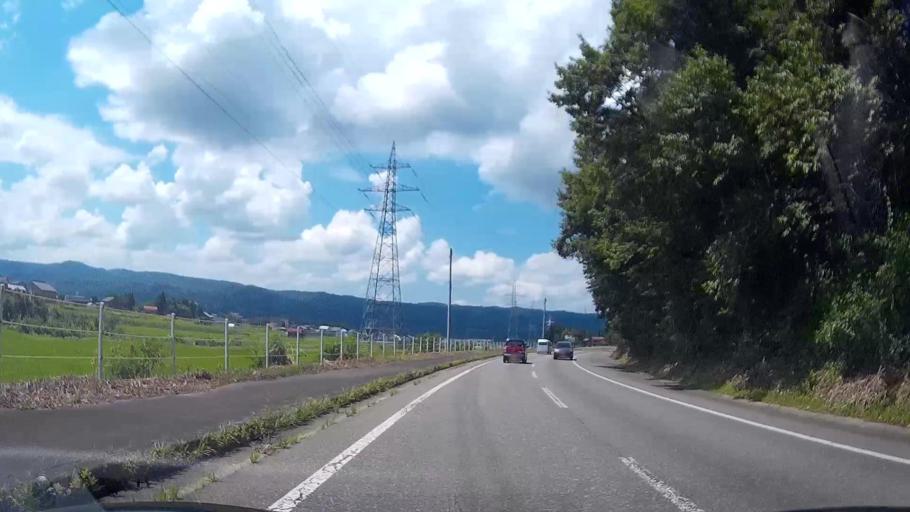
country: JP
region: Niigata
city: Tokamachi
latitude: 37.0964
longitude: 138.7407
